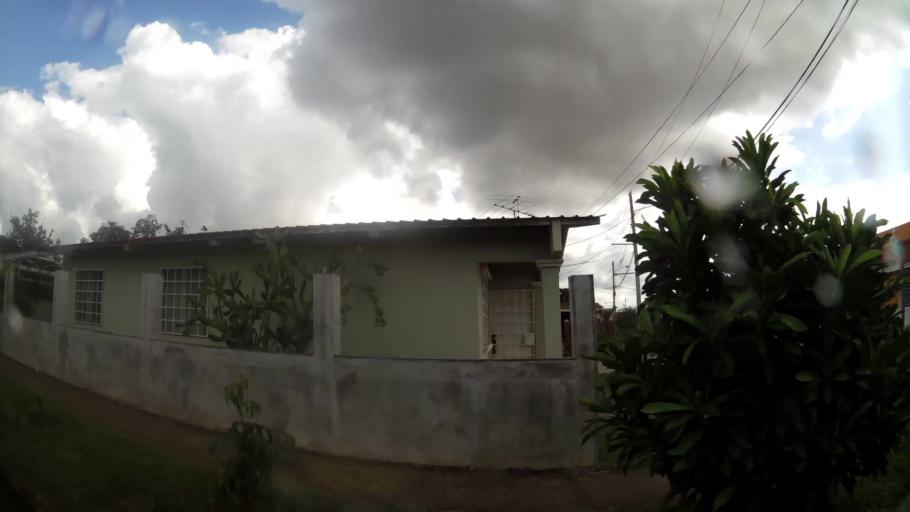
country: PA
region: Panama
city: Nuevo Arraijan
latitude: 8.9391
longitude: -79.7390
